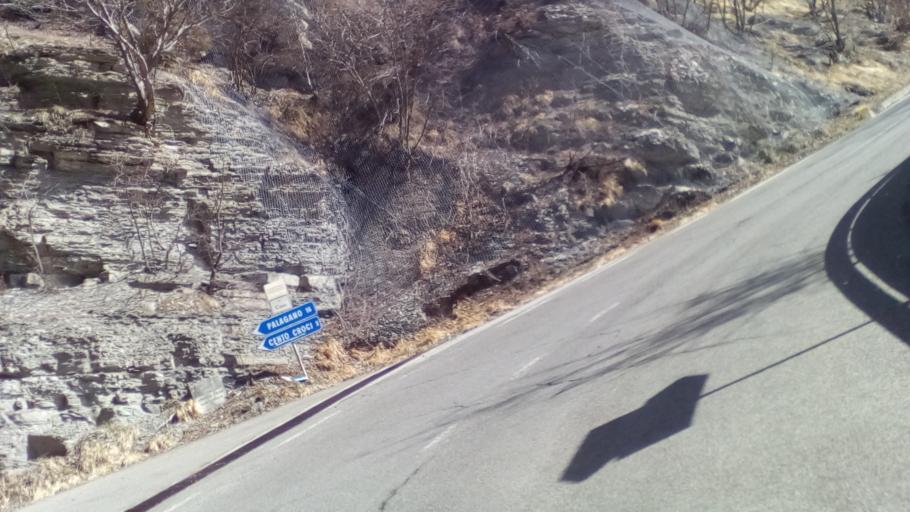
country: IT
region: Emilia-Romagna
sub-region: Provincia di Modena
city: Riolunato
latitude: 44.2562
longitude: 10.6347
